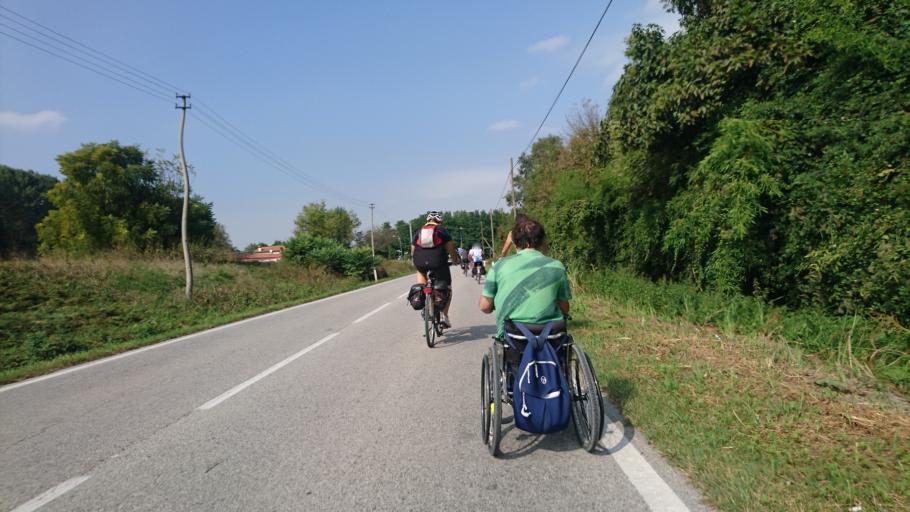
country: IT
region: Veneto
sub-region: Provincia di Padova
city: Grantorto
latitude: 45.5868
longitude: 11.7678
